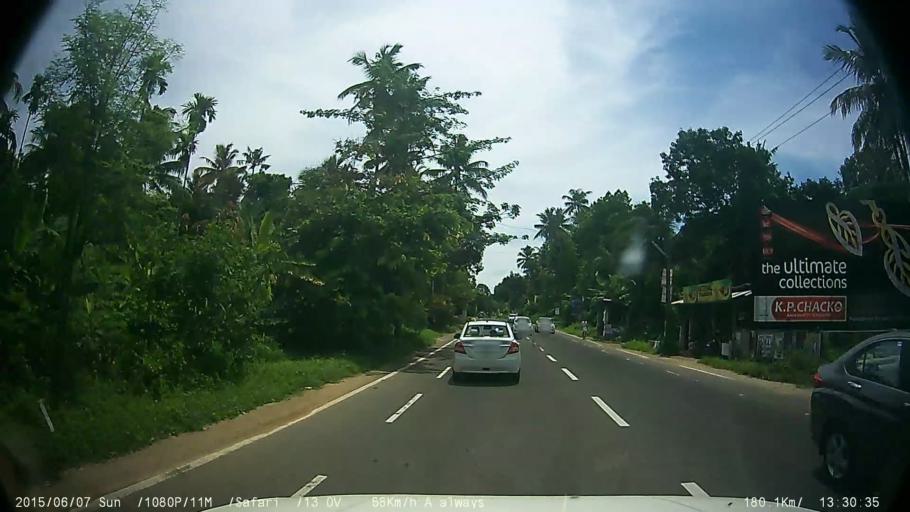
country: IN
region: Kerala
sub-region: Ernakulam
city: Muvattupula
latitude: 10.0370
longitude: 76.5437
